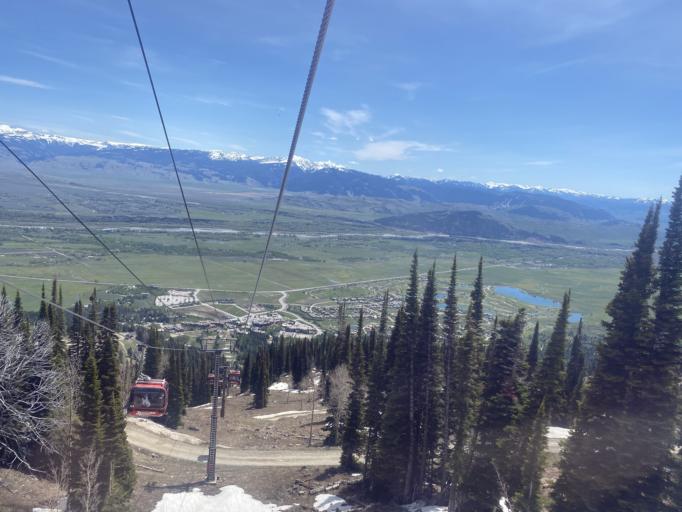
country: US
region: Wyoming
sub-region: Teton County
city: Moose Wilson Road
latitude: 43.5997
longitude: -110.8498
